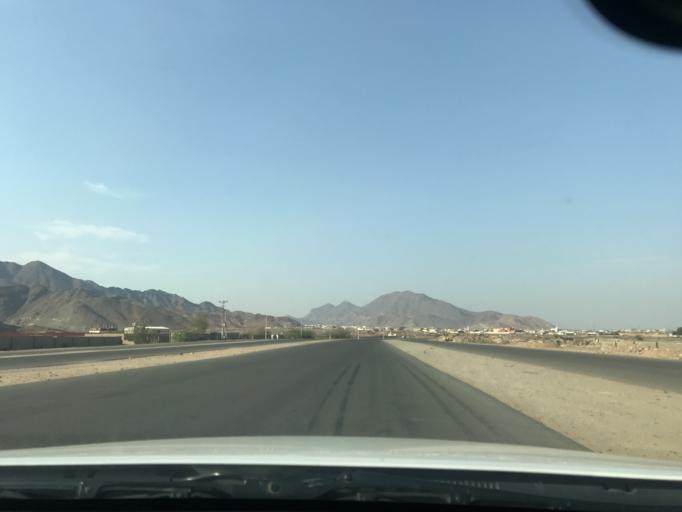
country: SA
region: Makkah
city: Al Jumum
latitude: 21.4478
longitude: 39.5205
